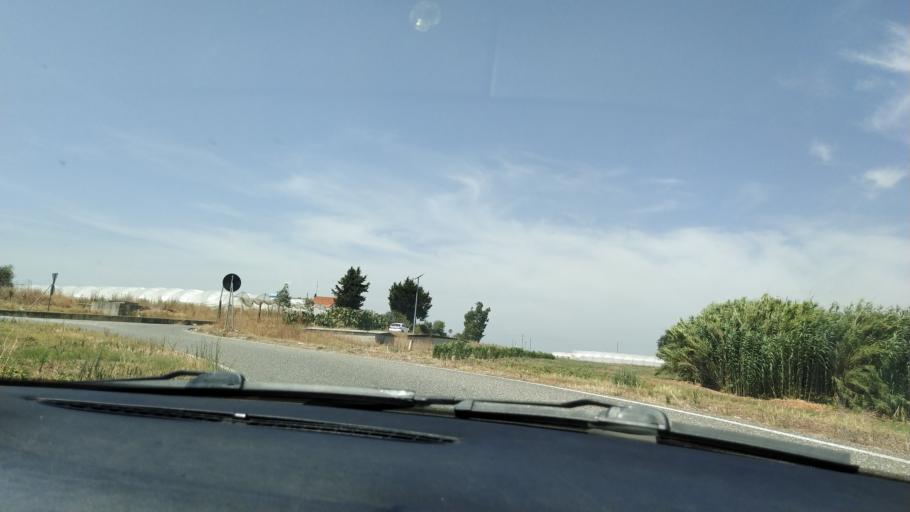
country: IT
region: Basilicate
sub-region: Provincia di Matera
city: Marconia
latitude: 40.3418
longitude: 16.7594
